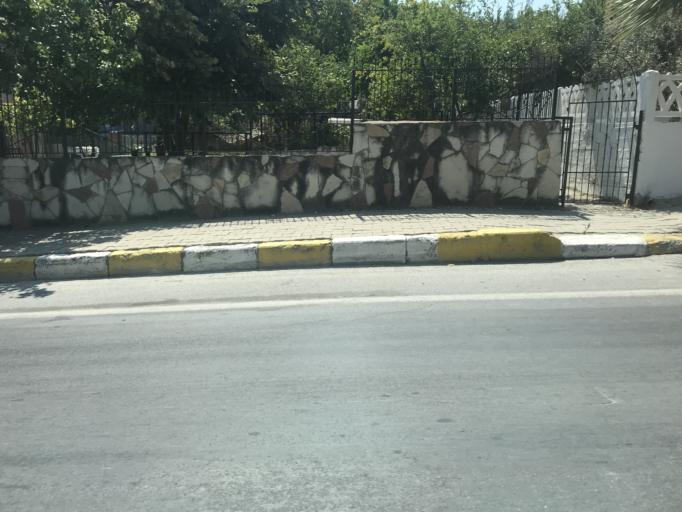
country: TR
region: Izmir
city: Urla
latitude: 38.3273
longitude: 26.7575
